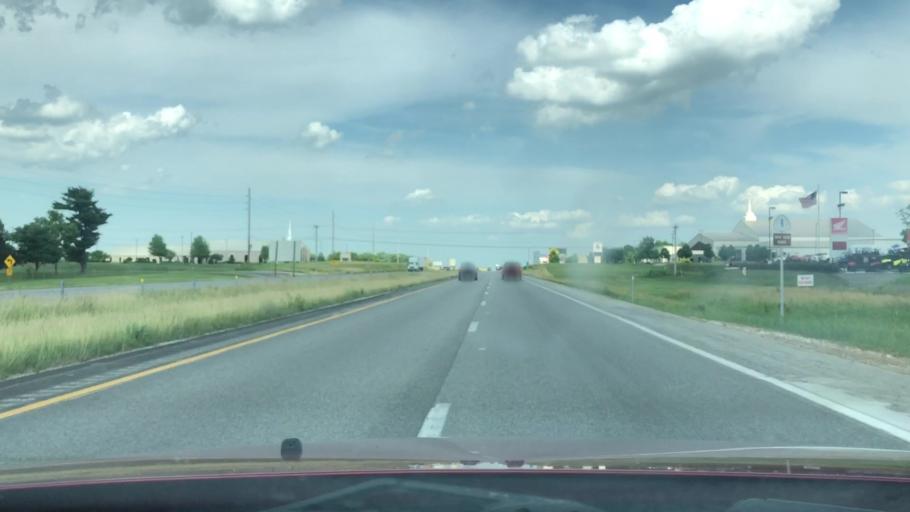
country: US
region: Missouri
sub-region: Greene County
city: Springfield
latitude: 37.2501
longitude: -93.2540
